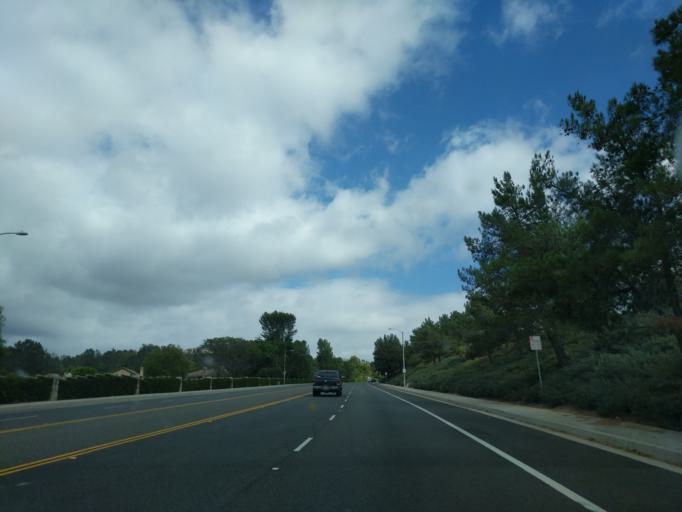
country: US
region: California
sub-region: Orange County
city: Laguna Woods
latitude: 33.5979
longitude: -117.7445
